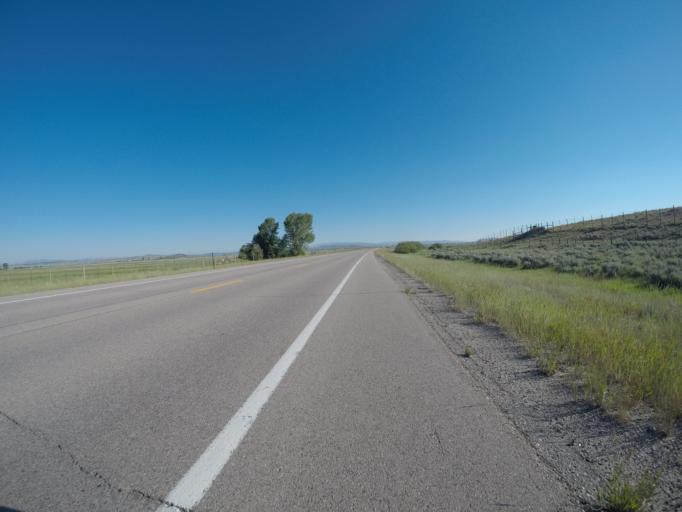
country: US
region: Wyoming
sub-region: Sublette County
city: Pinedale
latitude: 42.9516
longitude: -110.0862
